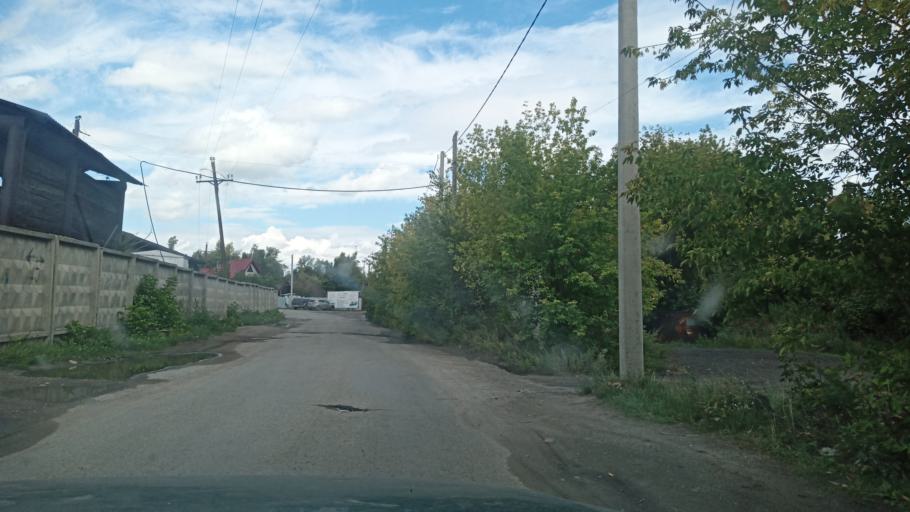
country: RU
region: Altai Krai
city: Zaton
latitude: 53.3335
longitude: 83.8069
